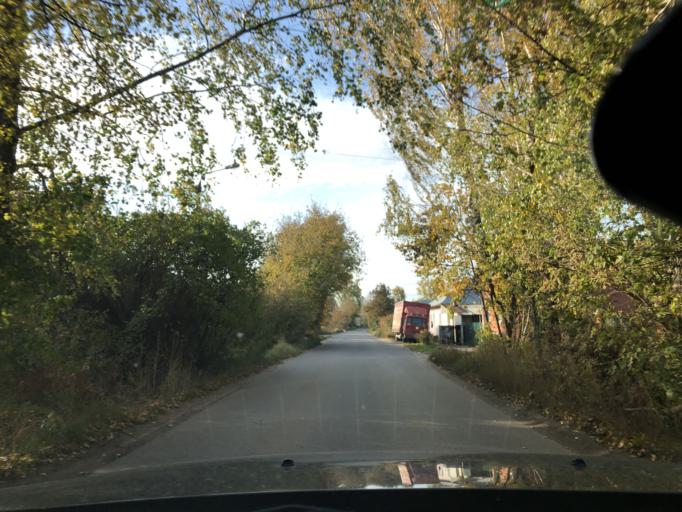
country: RU
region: Tula
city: Tula
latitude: 54.1879
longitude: 37.6362
